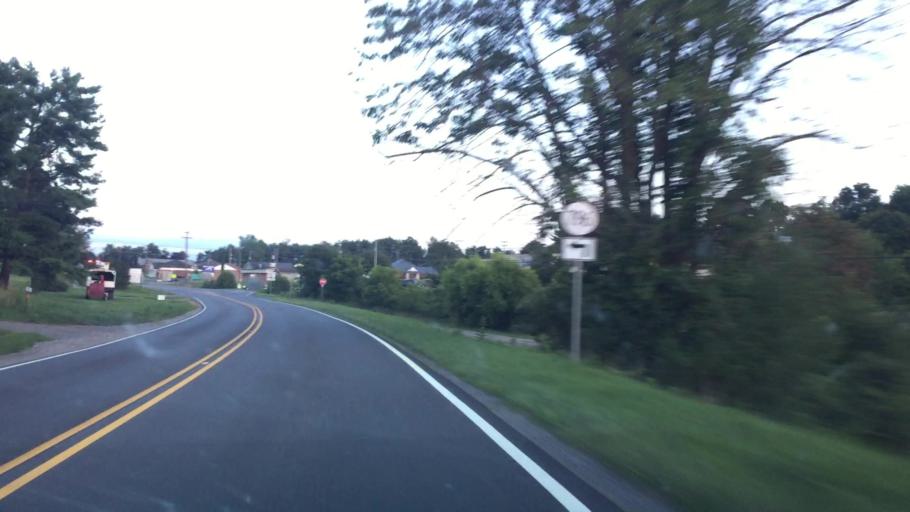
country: US
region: Virginia
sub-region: Wythe County
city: Wytheville
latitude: 36.9322
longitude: -80.9438
